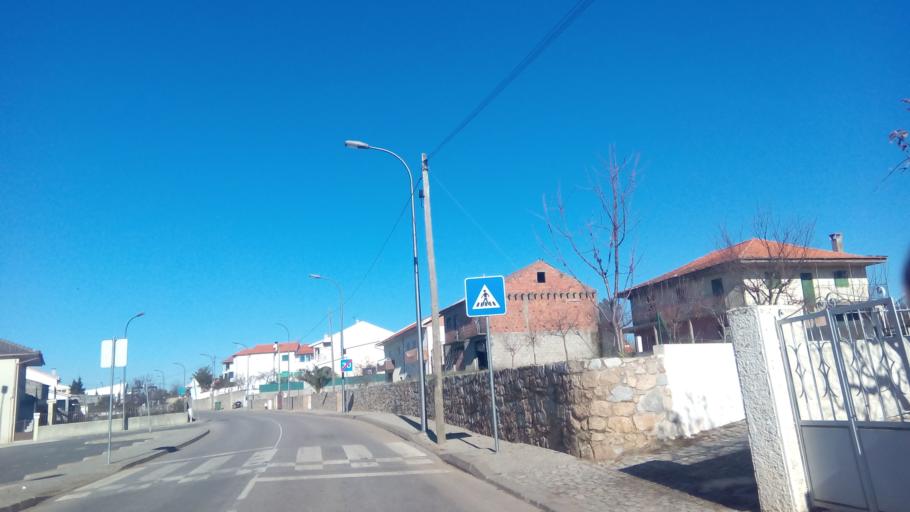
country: PT
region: Braganca
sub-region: Vimioso
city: Vimioso
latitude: 41.6363
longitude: -6.6022
